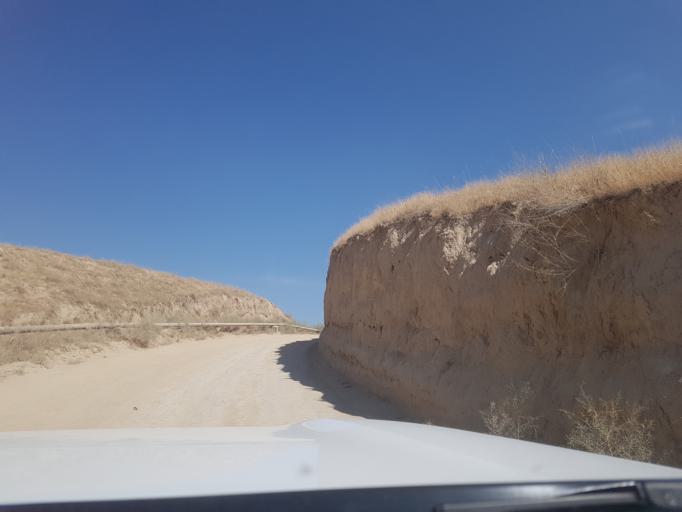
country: TM
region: Ahal
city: Baharly
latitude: 38.2728
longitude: 56.8955
